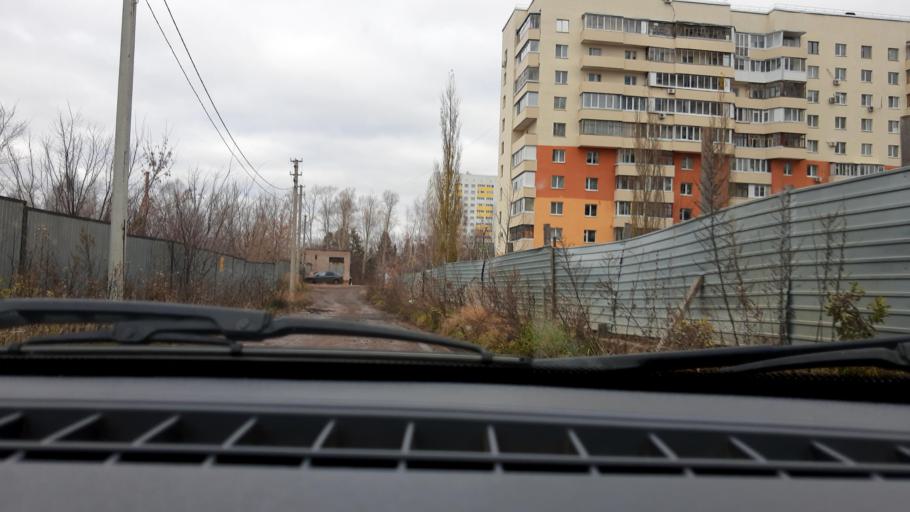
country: RU
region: Bashkortostan
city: Mikhaylovka
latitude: 54.7892
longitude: 55.8677
